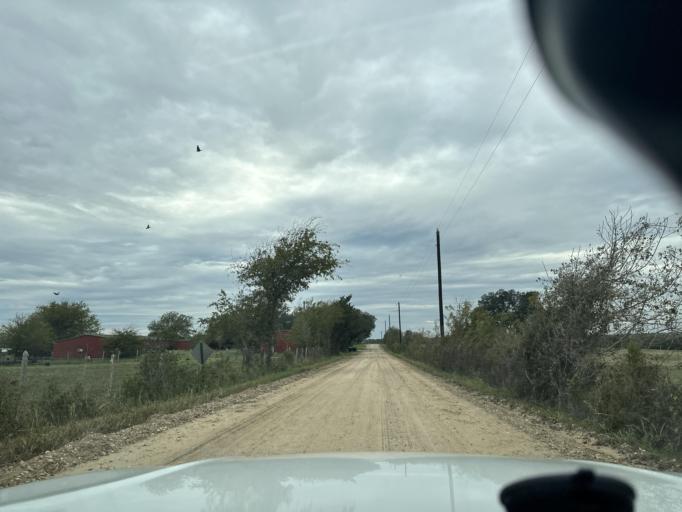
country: US
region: Texas
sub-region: Burleson County
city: Somerville
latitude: 30.1654
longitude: -96.6446
